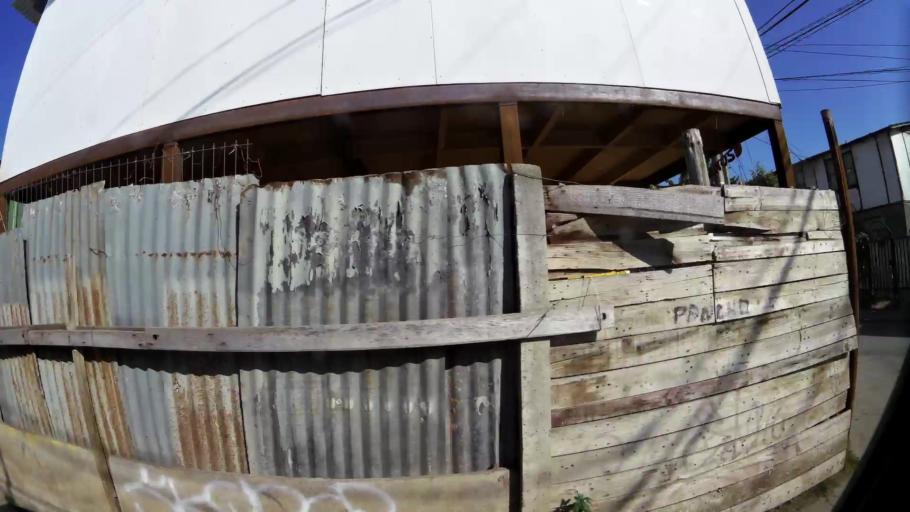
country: CL
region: Santiago Metropolitan
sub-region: Provincia de Santiago
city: Lo Prado
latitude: -33.4549
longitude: -70.7586
